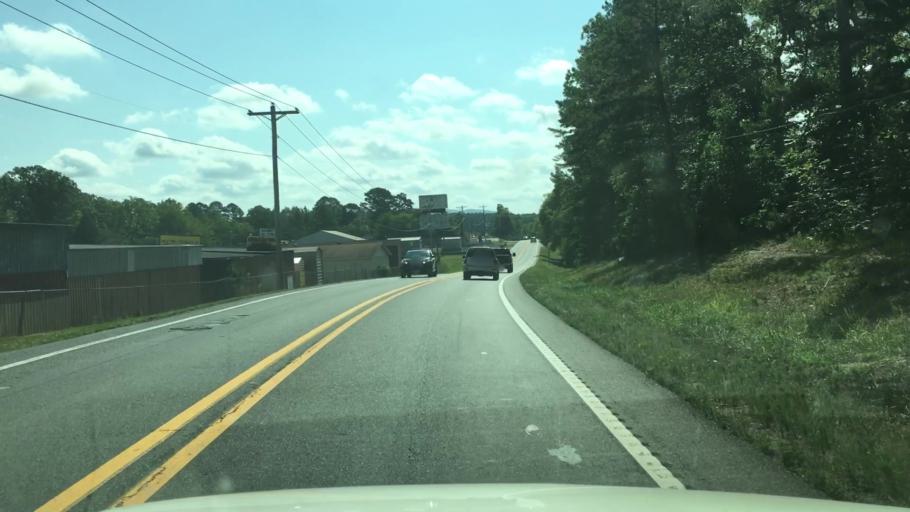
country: US
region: Arkansas
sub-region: Garland County
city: Piney
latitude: 34.5105
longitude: -93.2045
